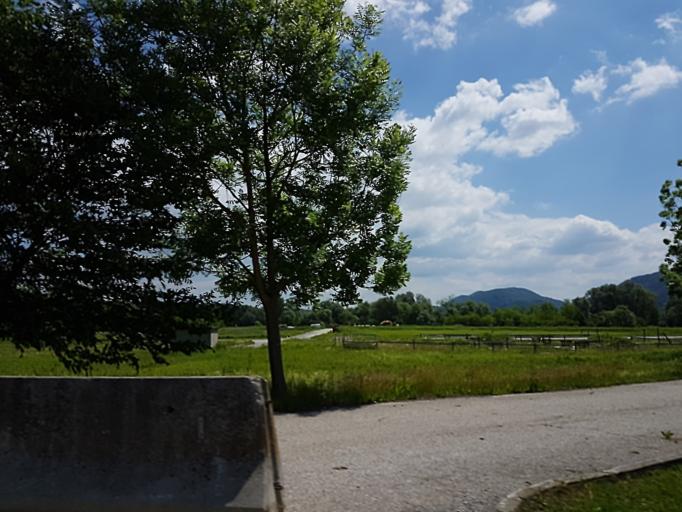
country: SI
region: Bistrica ob Sotli
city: Bistrica ob Sotli
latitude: 46.0724
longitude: 15.6613
